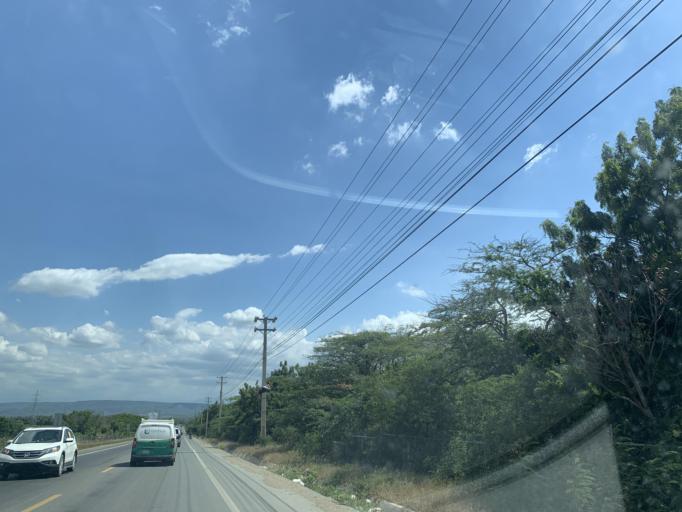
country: DO
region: Santiago
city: Villa Bisono
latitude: 19.5676
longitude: -70.8567
